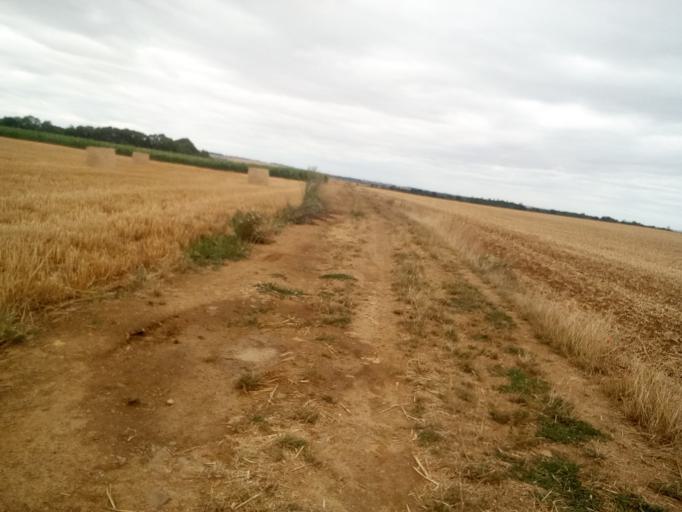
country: FR
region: Lower Normandy
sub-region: Departement du Calvados
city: Clinchamps-sur-Orne
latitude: 49.0607
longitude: -0.4130
